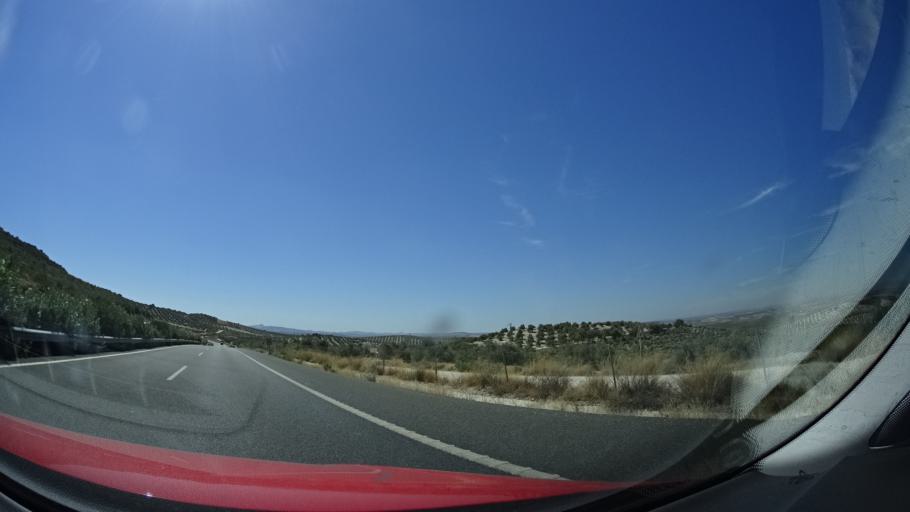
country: ES
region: Andalusia
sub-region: Provincia de Sevilla
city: Estepa
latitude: 37.2888
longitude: -4.9096
